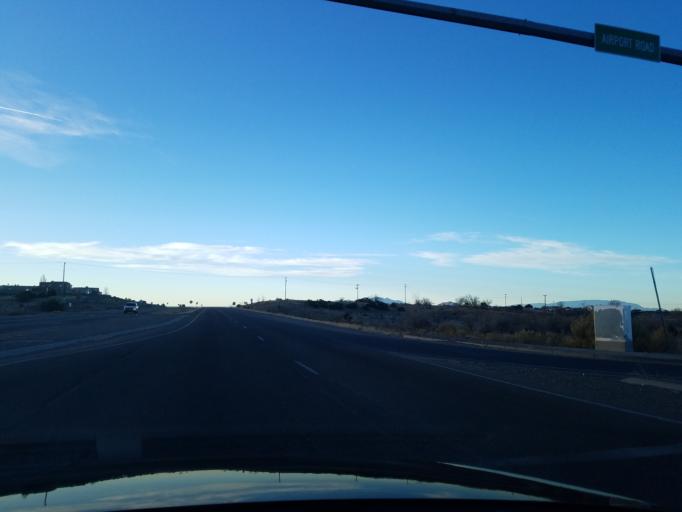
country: US
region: New Mexico
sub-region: Santa Fe County
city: Agua Fria
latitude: 35.6318
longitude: -106.0712
